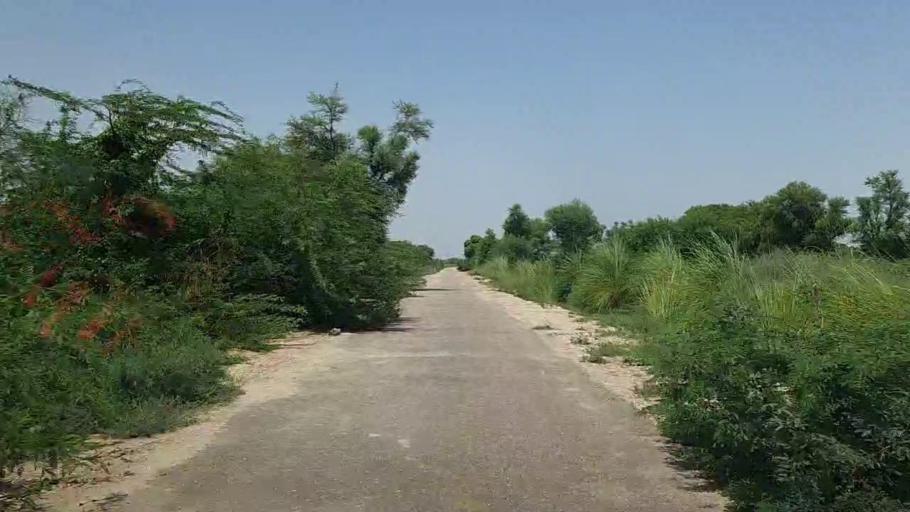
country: PK
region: Sindh
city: Pad Idan
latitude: 26.7436
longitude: 68.3139
